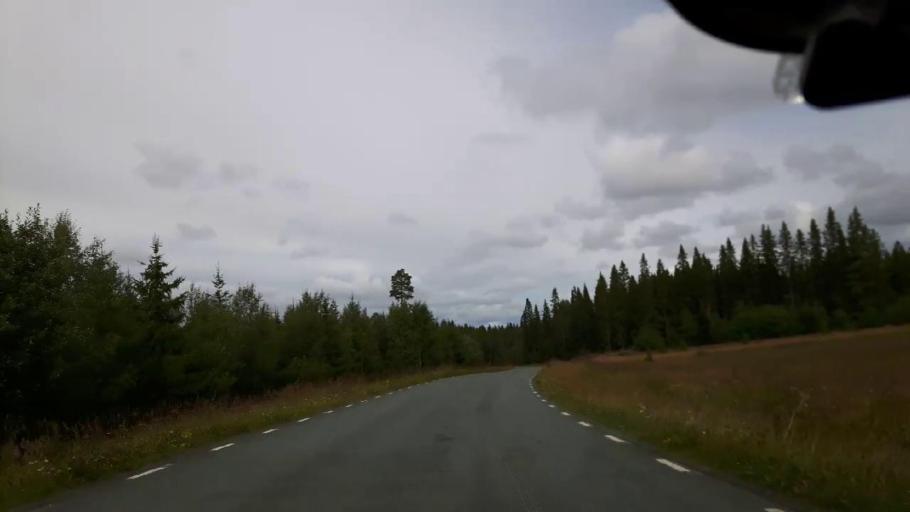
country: SE
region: Jaemtland
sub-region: Krokoms Kommun
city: Valla
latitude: 63.4566
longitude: 14.0427
